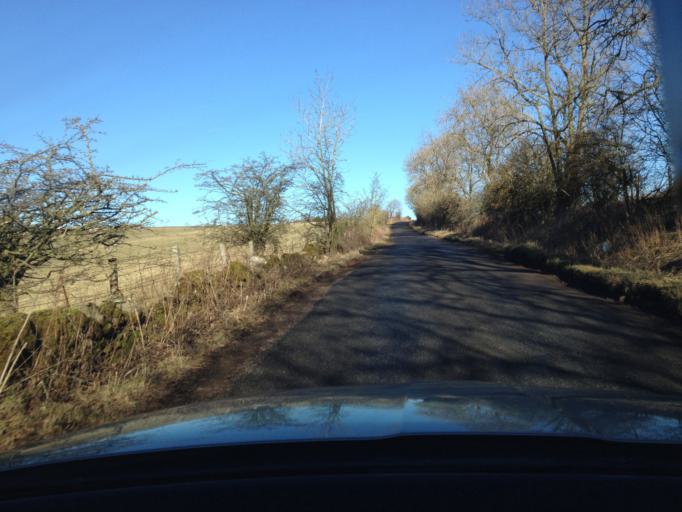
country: GB
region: Scotland
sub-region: Perth and Kinross
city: Bridge of Earn
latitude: 56.2943
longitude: -3.3973
